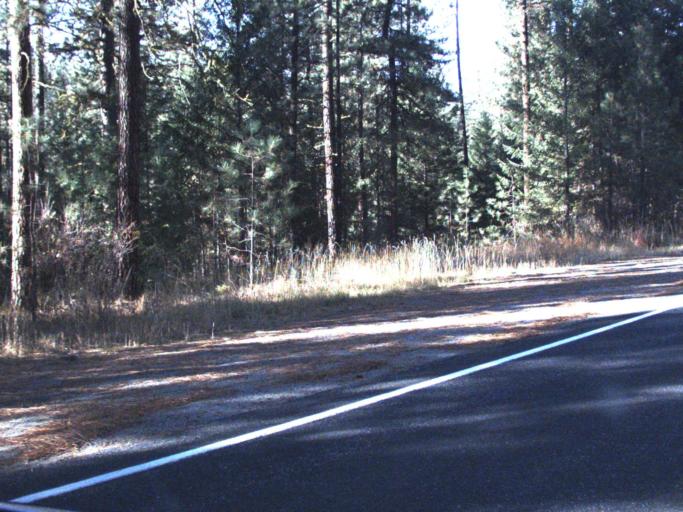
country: US
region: Washington
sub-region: Stevens County
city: Kettle Falls
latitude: 48.1880
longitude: -118.1706
